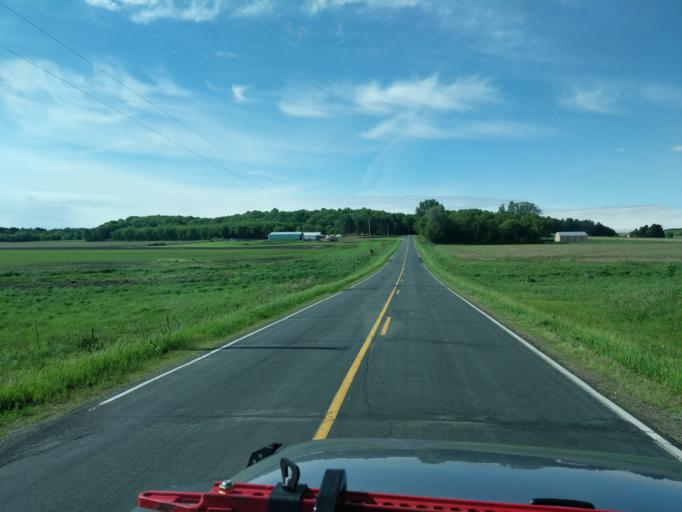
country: US
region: Wisconsin
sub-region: Saint Croix County
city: Hammond
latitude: 44.8873
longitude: -92.4864
